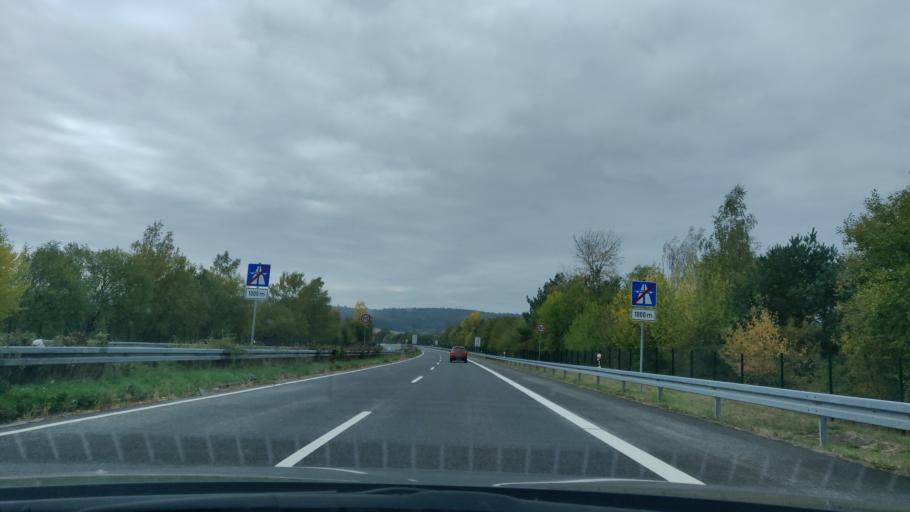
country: DE
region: Hesse
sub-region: Regierungsbezirk Kassel
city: Neuental
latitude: 51.0102
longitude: 9.2100
